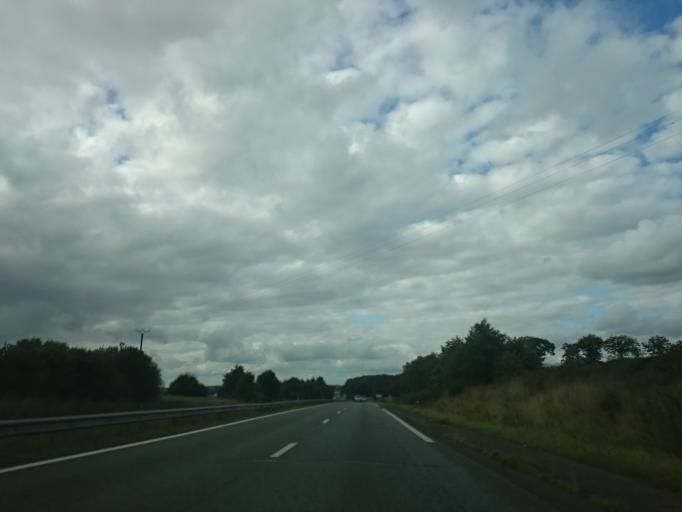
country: FR
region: Brittany
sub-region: Departement d'Ille-et-Vilaine
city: Quedillac
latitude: 48.2417
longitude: -2.1288
